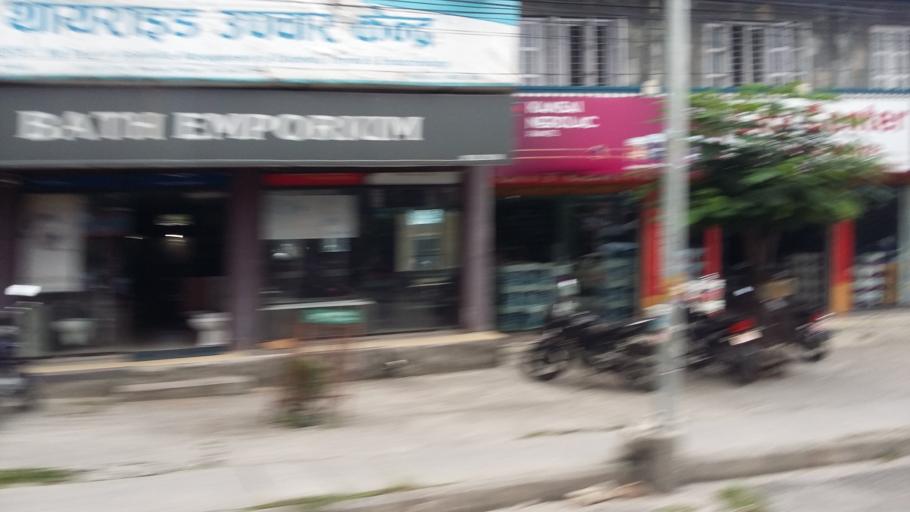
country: NP
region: Western Region
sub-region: Gandaki Zone
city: Pokhara
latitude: 28.2150
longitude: 83.9859
